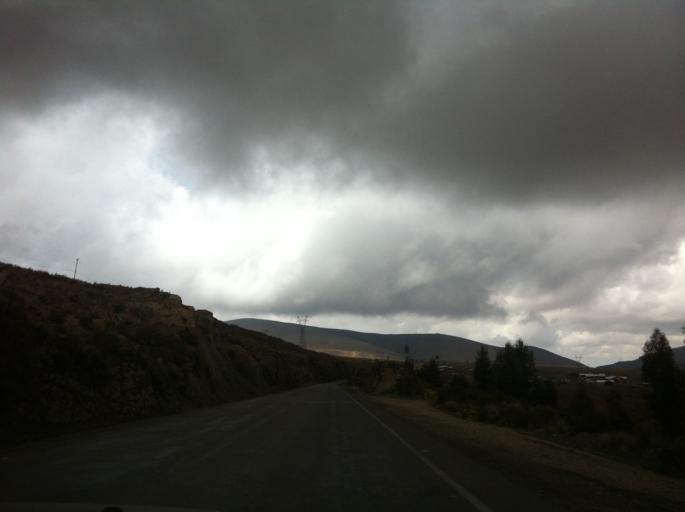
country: BO
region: Cochabamba
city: Irpa Irpa
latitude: -17.6947
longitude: -66.5169
